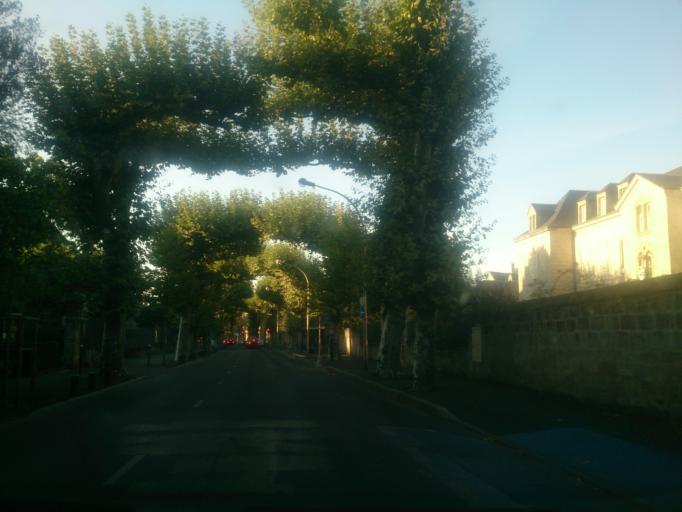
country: FR
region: Limousin
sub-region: Departement de la Correze
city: Brive-la-Gaillarde
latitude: 45.1579
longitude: 1.5361
